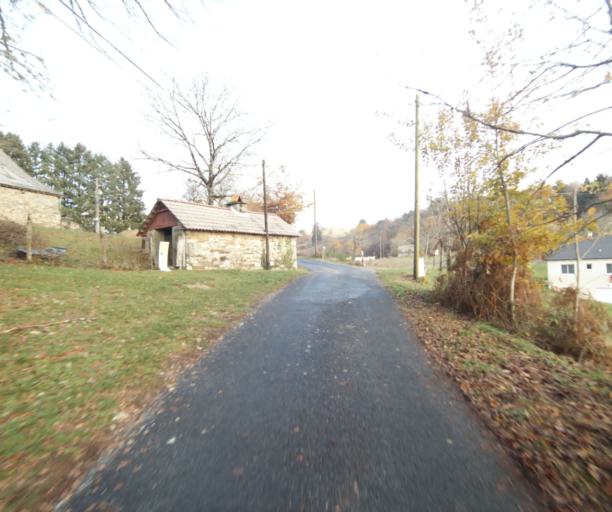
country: FR
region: Limousin
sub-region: Departement de la Correze
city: Cornil
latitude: 45.2037
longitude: 1.6985
